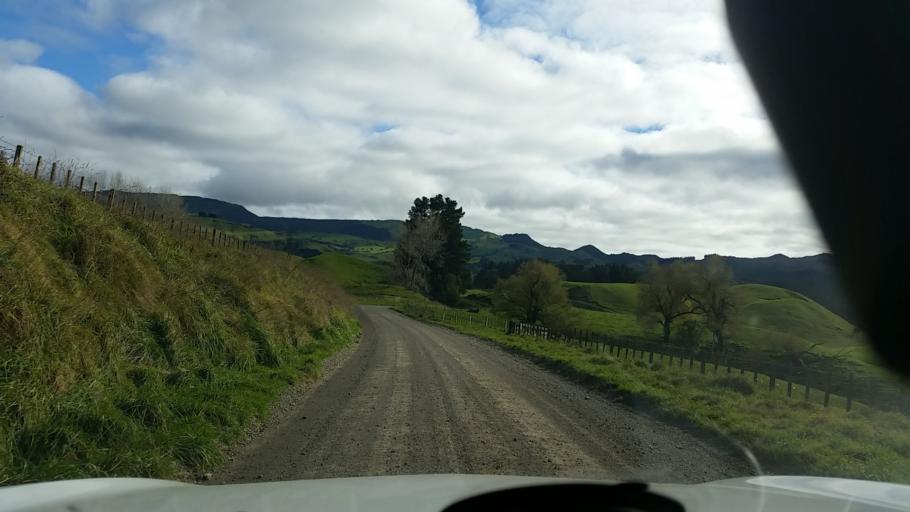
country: NZ
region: Hawke's Bay
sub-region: Napier City
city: Napier
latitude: -39.1087
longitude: 176.8925
